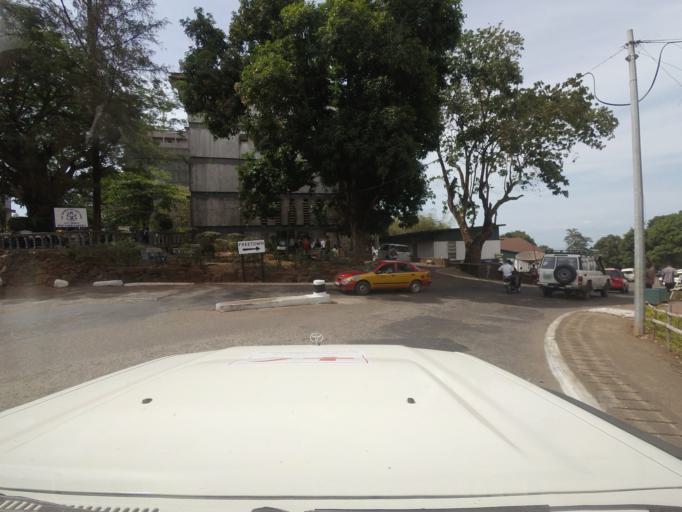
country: SL
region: Western Area
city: Freetown
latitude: 8.4771
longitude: -13.2212
